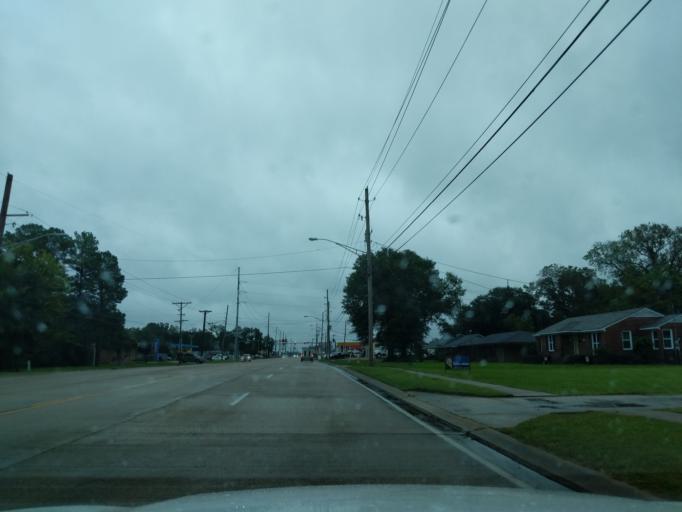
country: US
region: Louisiana
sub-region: Bossier Parish
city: Bossier City
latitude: 32.5207
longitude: -93.6984
